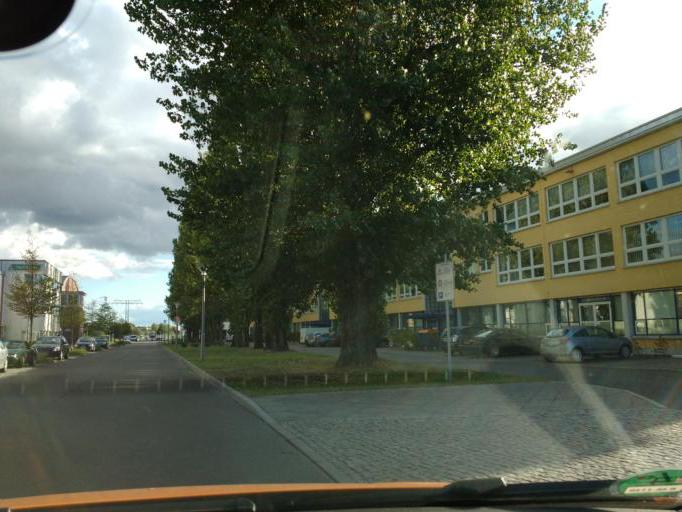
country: DE
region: Berlin
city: Johannisthal
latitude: 52.4301
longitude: 13.5221
